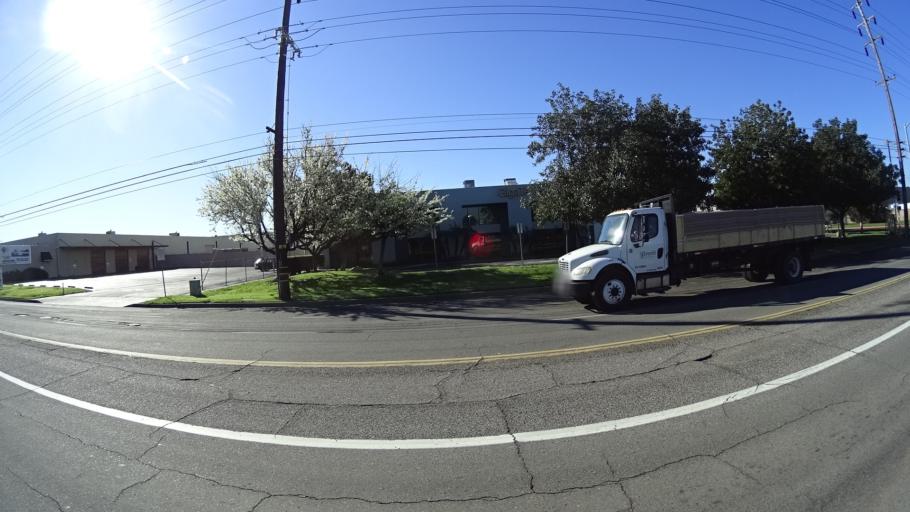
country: US
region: California
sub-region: Orange County
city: Fullerton
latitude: 33.8598
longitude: -117.8977
